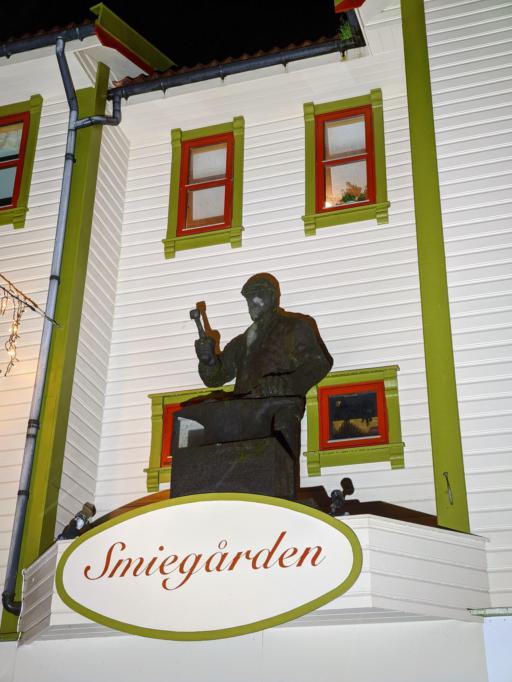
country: NO
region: Rogaland
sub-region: Time
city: Bryne
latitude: 58.7356
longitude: 5.6451
